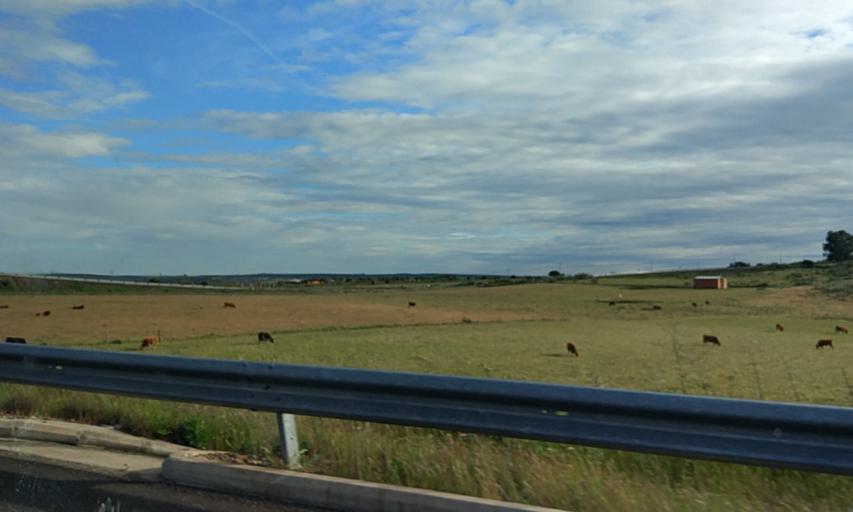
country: ES
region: Extremadura
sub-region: Provincia de Caceres
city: Casas de Don Gomez
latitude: 40.0172
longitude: -6.5885
